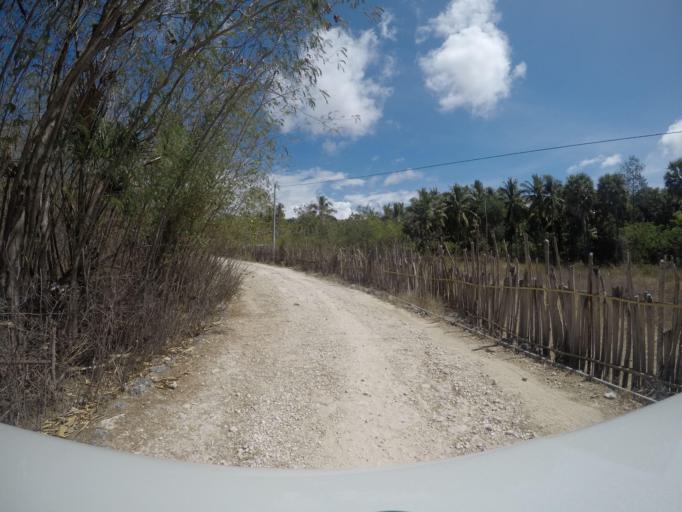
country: TL
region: Baucau
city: Baucau
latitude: -8.4456
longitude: 126.4374
